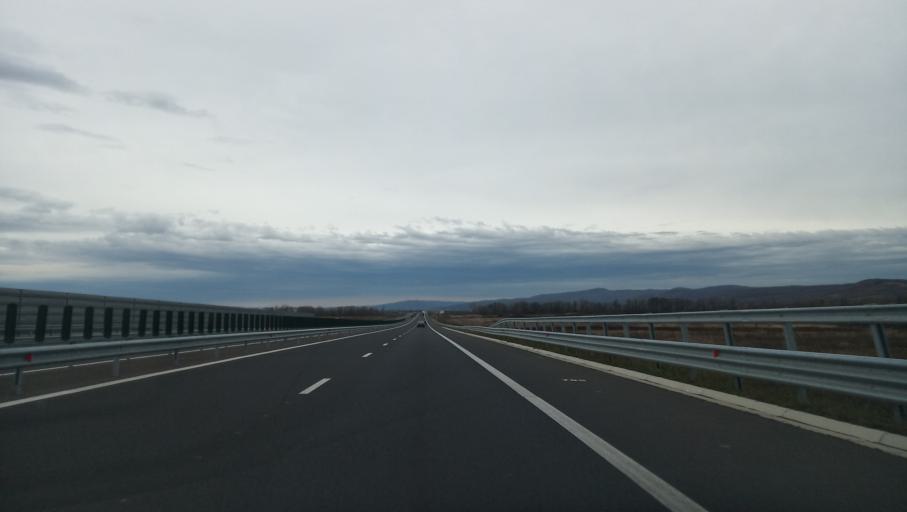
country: RO
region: Hunedoara
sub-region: Comuna Ilia
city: Ilia
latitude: 45.9472
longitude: 22.7046
